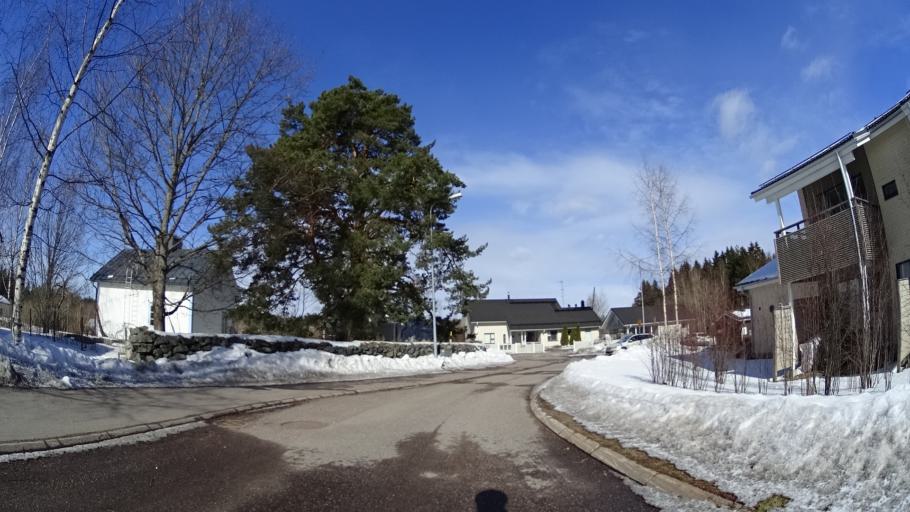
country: FI
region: Uusimaa
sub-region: Helsinki
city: Kauniainen
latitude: 60.2265
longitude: 24.6984
